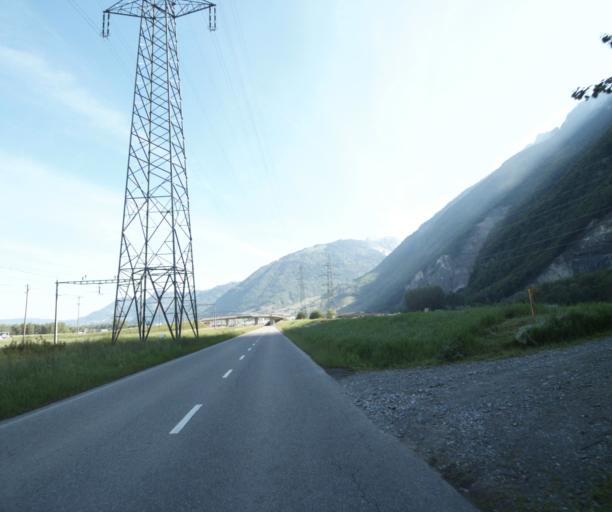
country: CH
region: Vaud
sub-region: Aigle District
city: Villeneuve
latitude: 46.3753
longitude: 6.9271
